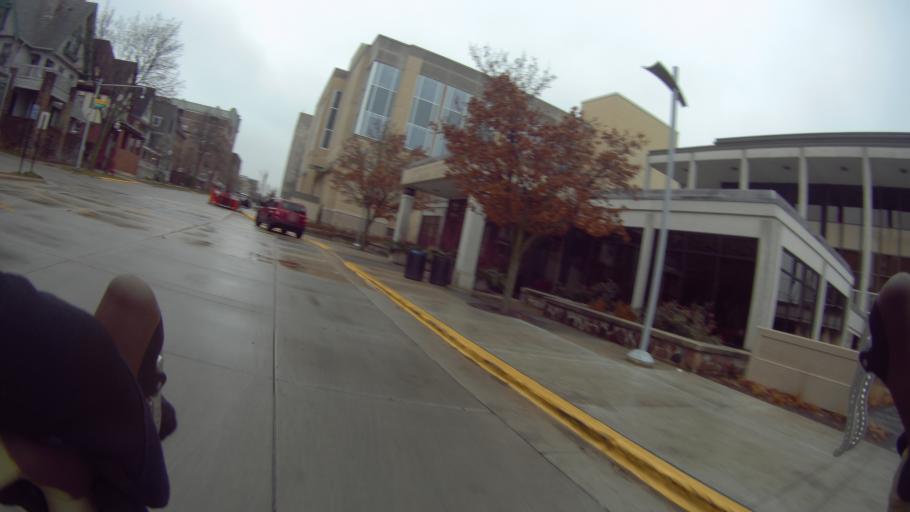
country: US
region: Wisconsin
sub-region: Dane County
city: Madison
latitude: 43.0769
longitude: -89.3975
